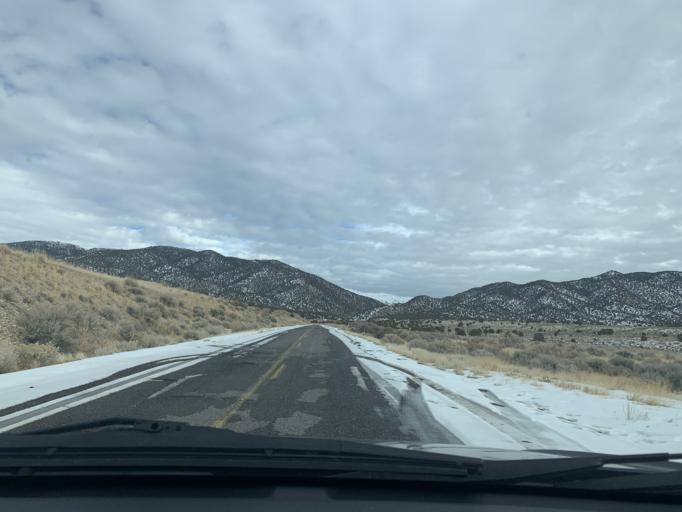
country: US
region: Utah
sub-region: Tooele County
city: Tooele
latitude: 40.2996
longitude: -112.2707
